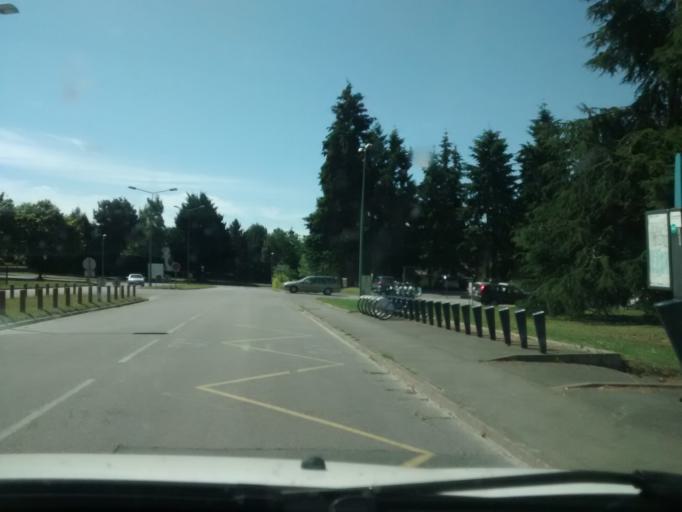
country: FR
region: Brittany
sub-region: Departement d'Ille-et-Vilaine
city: Cesson-Sevigne
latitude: 48.1165
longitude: -1.6339
